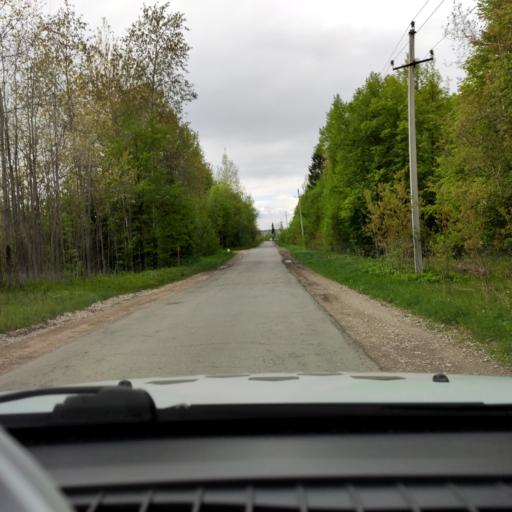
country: RU
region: Perm
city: Novyye Lyady
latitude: 58.0417
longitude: 56.6219
